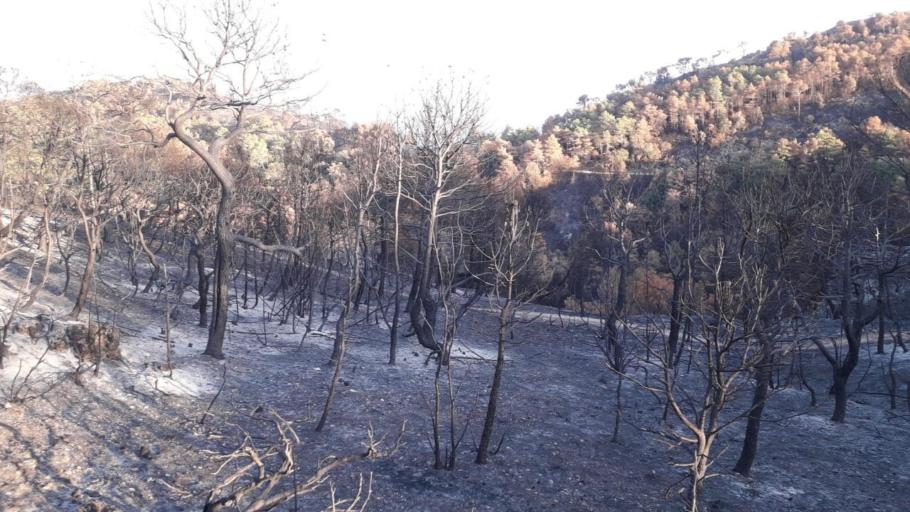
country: ES
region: Catalonia
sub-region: Provincia de Barcelona
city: Sant Marti de Tous
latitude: 41.5200
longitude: 1.4934
